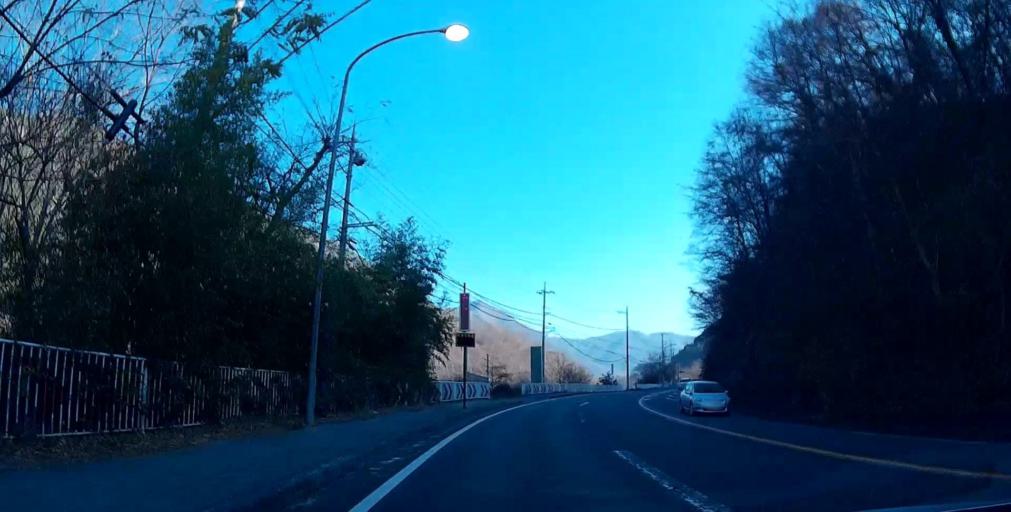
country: JP
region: Yamanashi
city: Fujikawaguchiko
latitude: 35.5894
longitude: 138.7341
